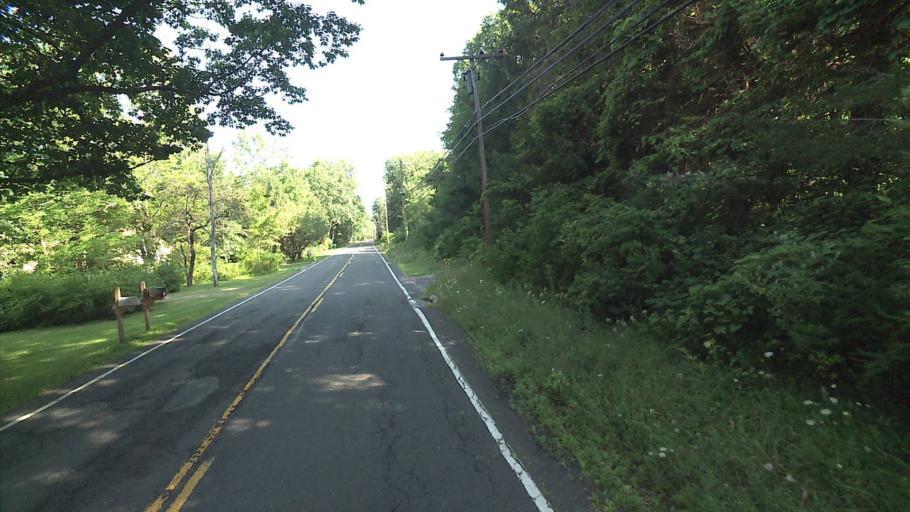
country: US
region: Connecticut
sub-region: Litchfield County
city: Winsted
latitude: 41.9584
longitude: -73.1021
